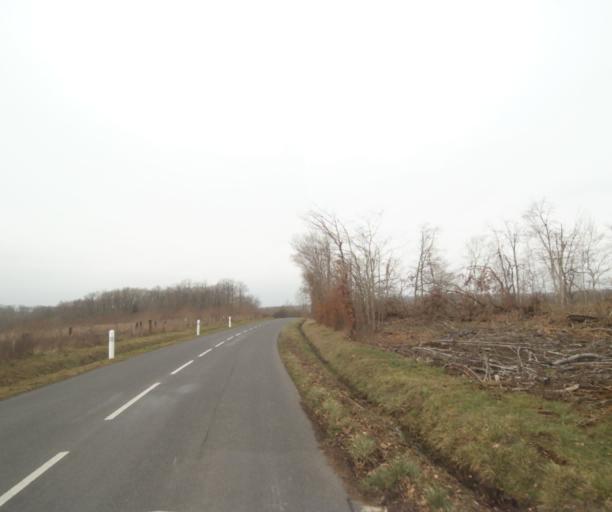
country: FR
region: Champagne-Ardenne
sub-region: Departement de la Marne
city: Pargny-sur-Saulx
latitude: 48.7364
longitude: 4.8834
